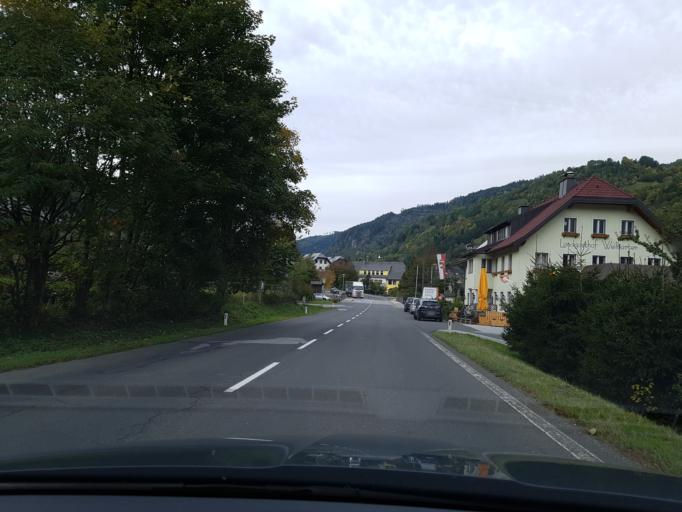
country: AT
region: Salzburg
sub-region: Politischer Bezirk Tamsweg
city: Ramingstein
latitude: 47.0679
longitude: 13.8842
